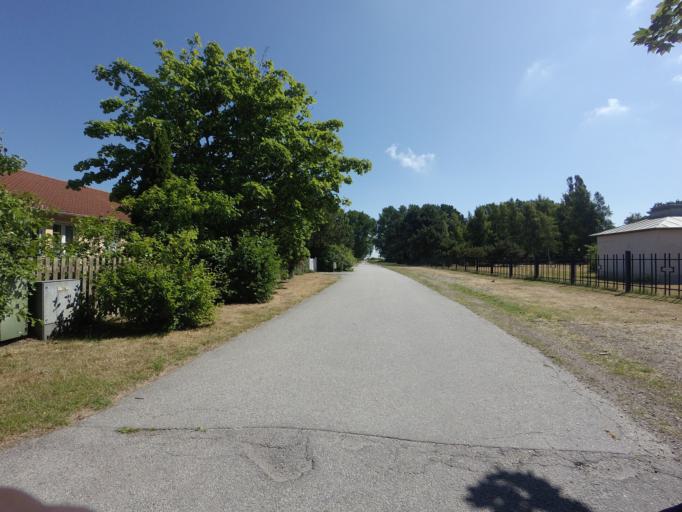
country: SE
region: Skane
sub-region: Vellinge Kommun
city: Skanor med Falsterbo
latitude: 55.4202
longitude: 12.8554
